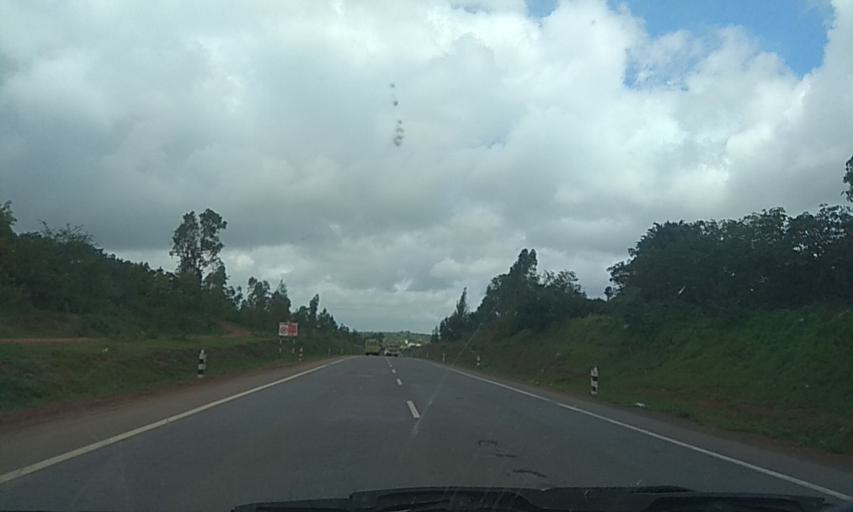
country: IN
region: Karnataka
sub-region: Dharwad
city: Hubli
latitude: 15.4486
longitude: 74.9684
